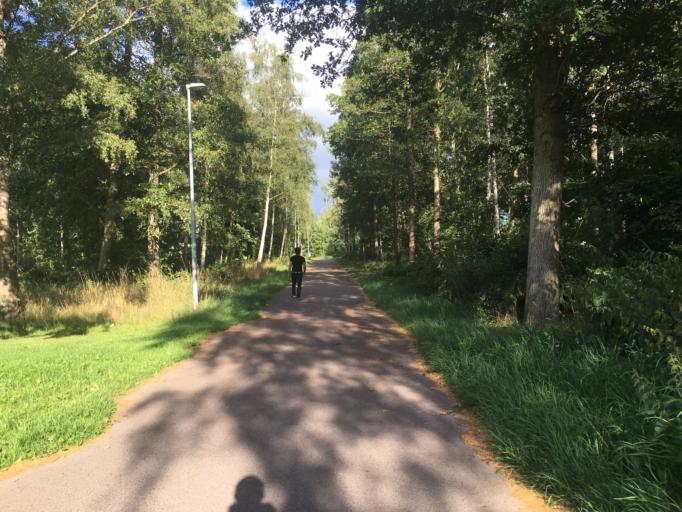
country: SE
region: Kalmar
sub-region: Kalmar Kommun
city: Kalmar
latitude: 56.7037
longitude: 16.3622
